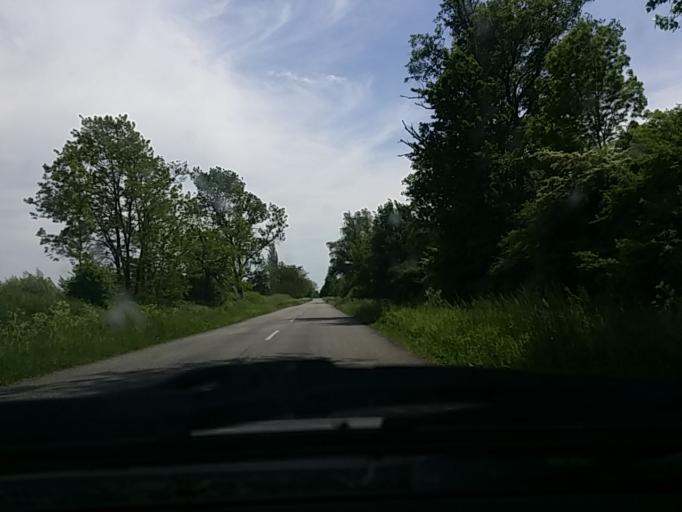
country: HU
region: Baranya
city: Szigetvar
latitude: 45.9248
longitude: 17.6597
